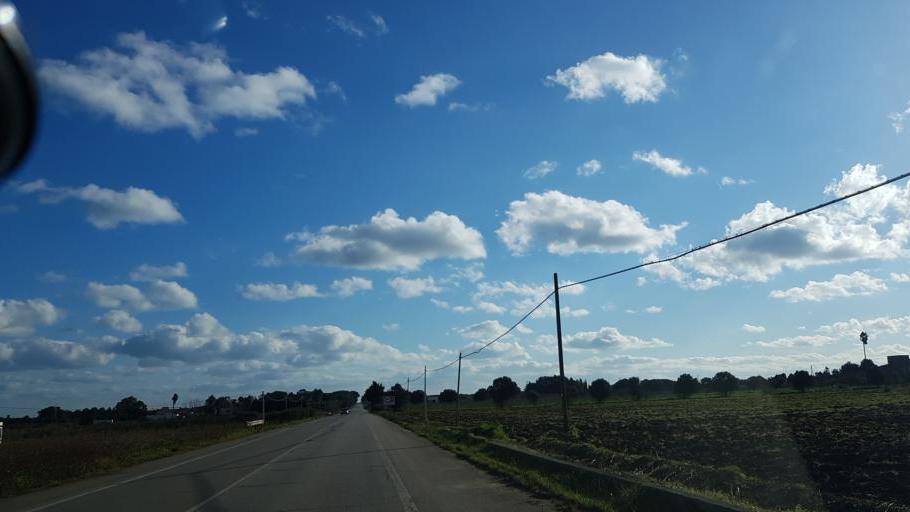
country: IT
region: Apulia
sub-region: Provincia di Brindisi
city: Brindisi
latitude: 40.6467
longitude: 17.8877
